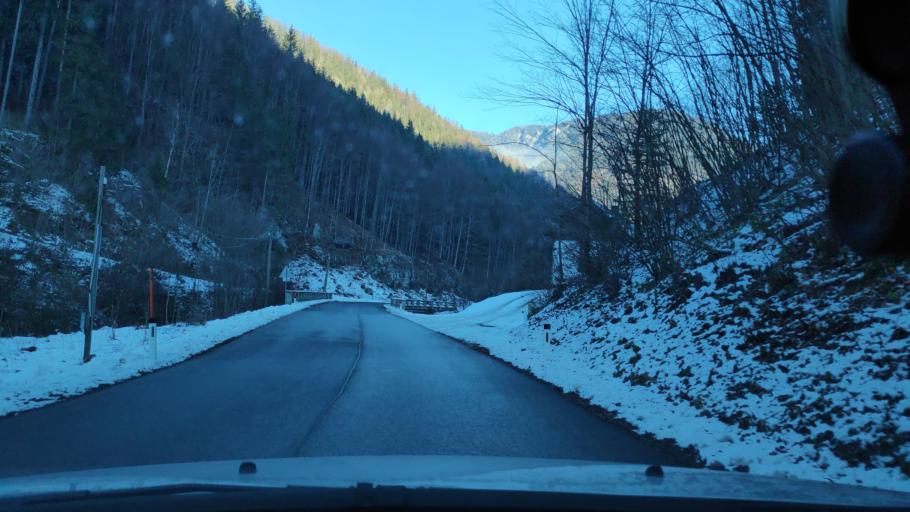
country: AT
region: Lower Austria
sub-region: Politischer Bezirk Neunkirchen
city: Schwarzau im Gebirge
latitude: 47.7697
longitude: 15.7186
